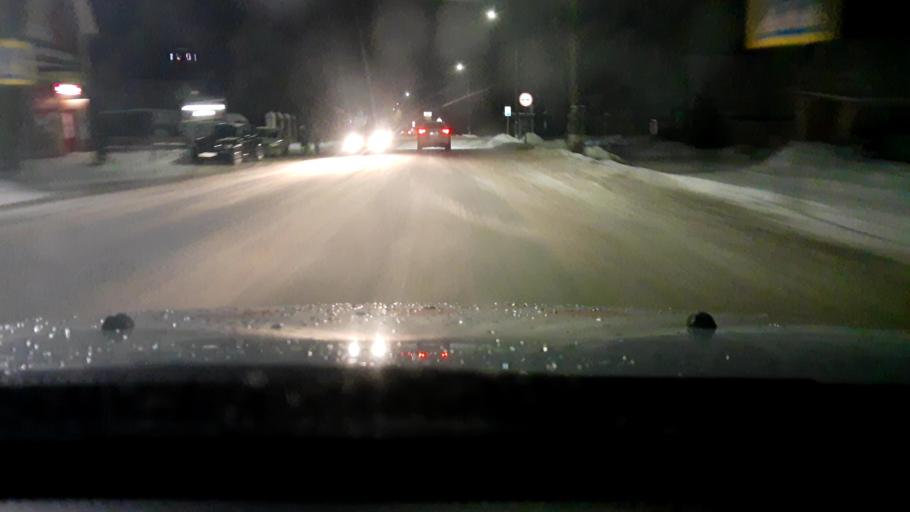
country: RU
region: Nizjnij Novgorod
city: Gorodets
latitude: 56.6622
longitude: 43.4693
